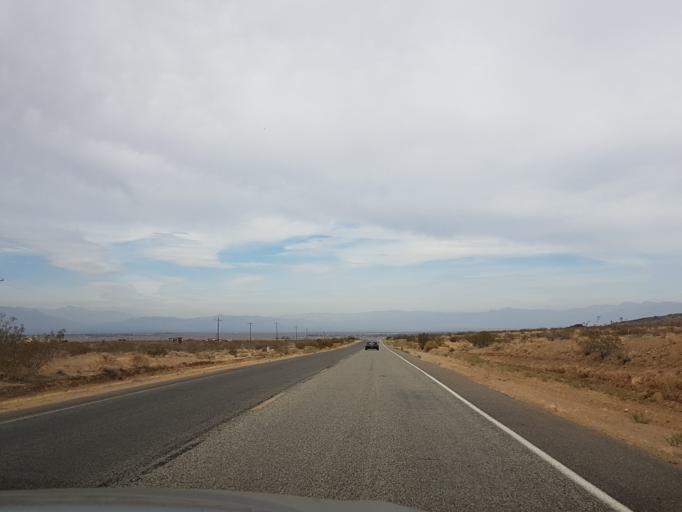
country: US
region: California
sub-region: Kern County
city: Ridgecrest
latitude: 35.5642
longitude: -117.7138
